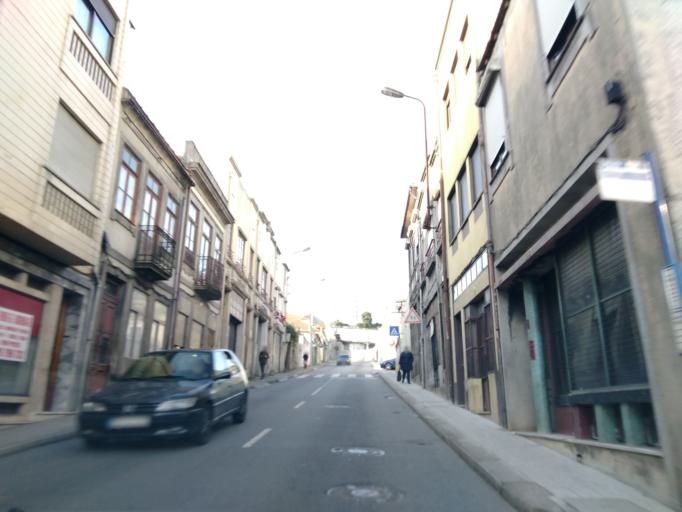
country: PT
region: Porto
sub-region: Vila Nova de Gaia
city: Oliveira do Douro
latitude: 41.1457
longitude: -8.5837
